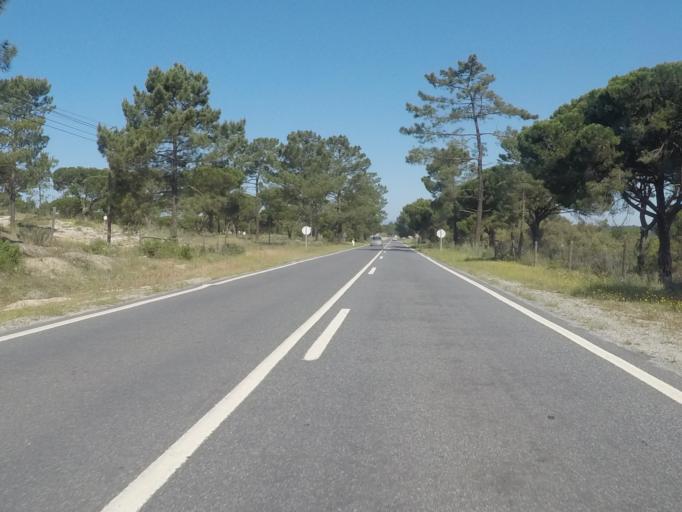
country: PT
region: Setubal
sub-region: Grandola
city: Grandola
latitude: 38.3047
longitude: -8.7369
